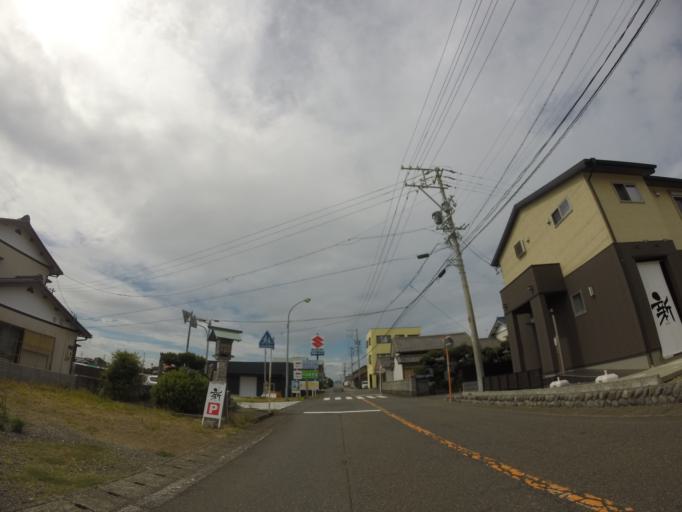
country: JP
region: Shizuoka
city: Oyama
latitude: 34.6224
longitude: 138.2008
